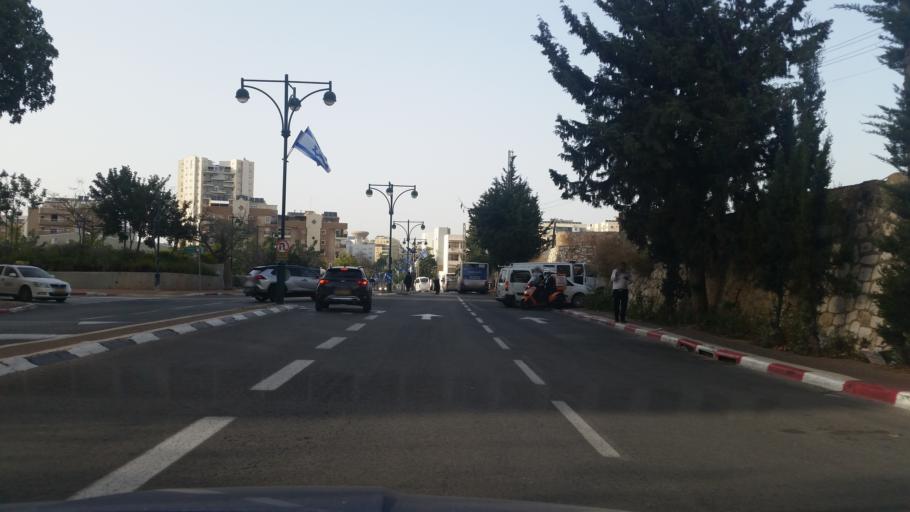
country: IL
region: Tel Aviv
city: Bene Beraq
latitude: 32.0719
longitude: 34.8329
